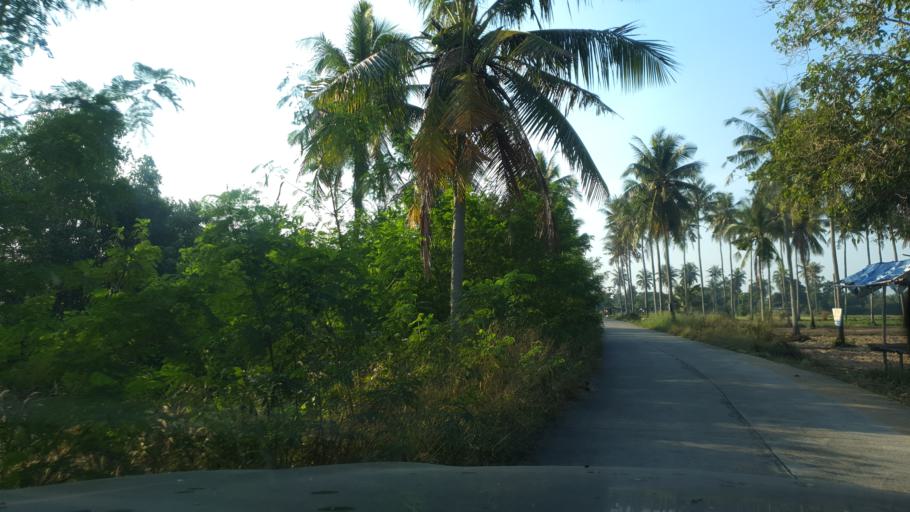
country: TH
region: Prachuap Khiri Khan
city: Bang Saphan
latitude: 11.2948
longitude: 99.5493
